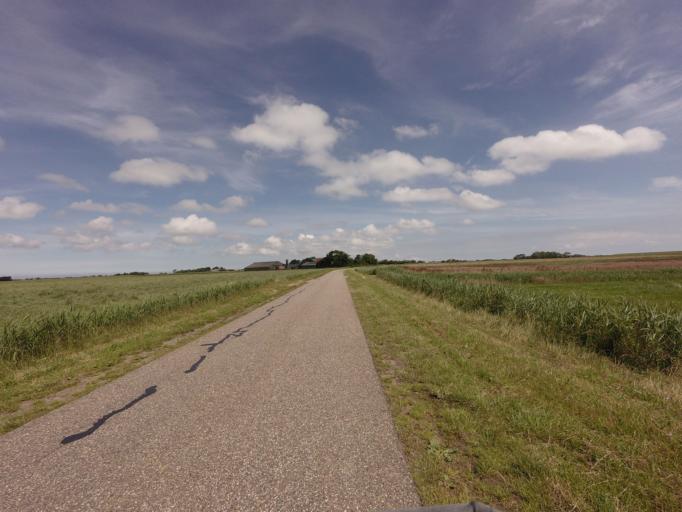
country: NL
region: North Holland
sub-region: Gemeente Texel
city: Den Burg
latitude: 53.0628
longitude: 4.8504
